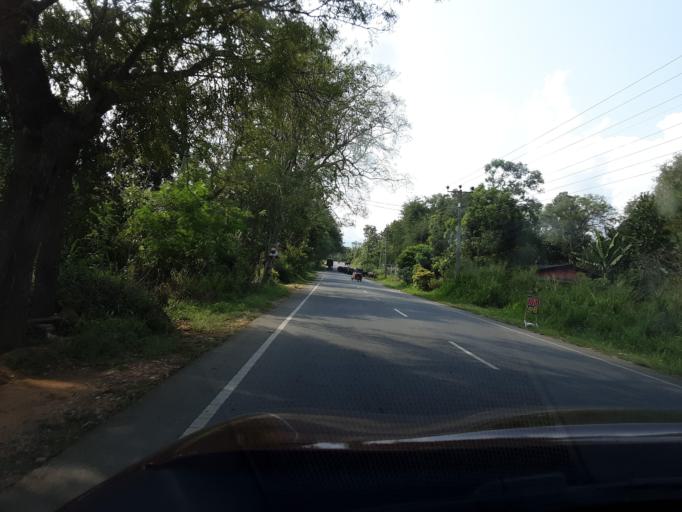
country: LK
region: Uva
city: Haputale
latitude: 6.6065
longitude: 81.1358
